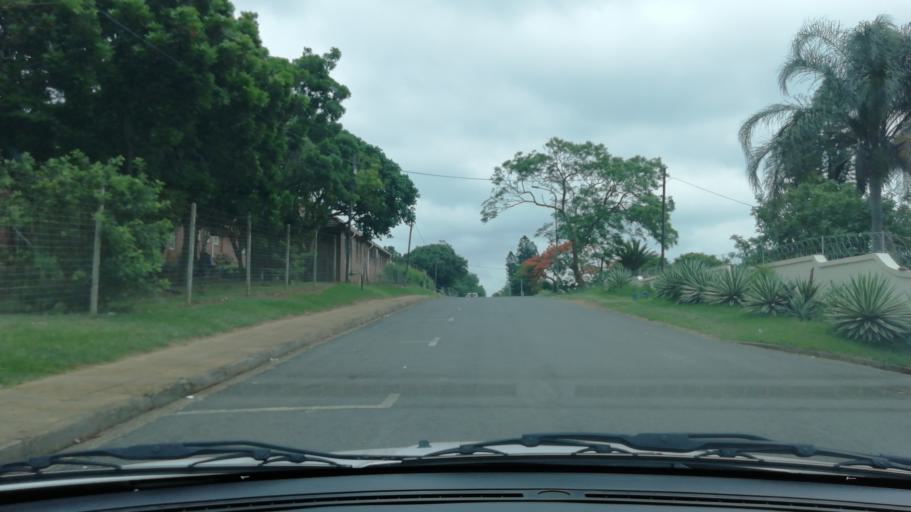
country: ZA
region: KwaZulu-Natal
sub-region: uThungulu District Municipality
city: Empangeni
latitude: -28.7481
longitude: 31.8919
